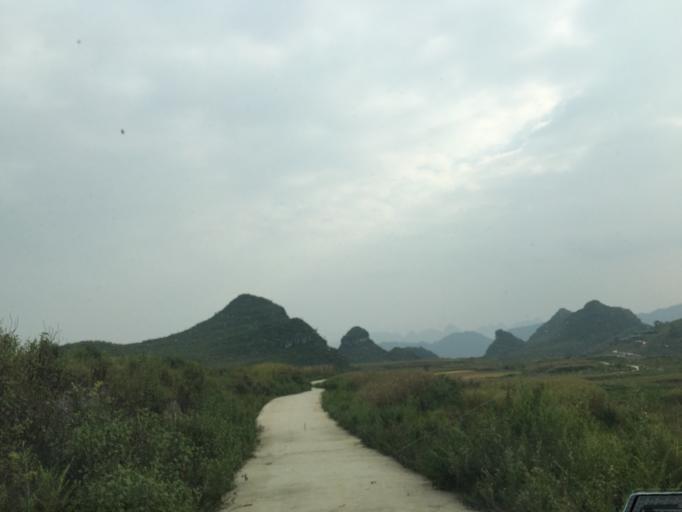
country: CN
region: Guangxi Zhuangzu Zizhiqu
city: Xinzhou
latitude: 25.4433
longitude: 105.6421
